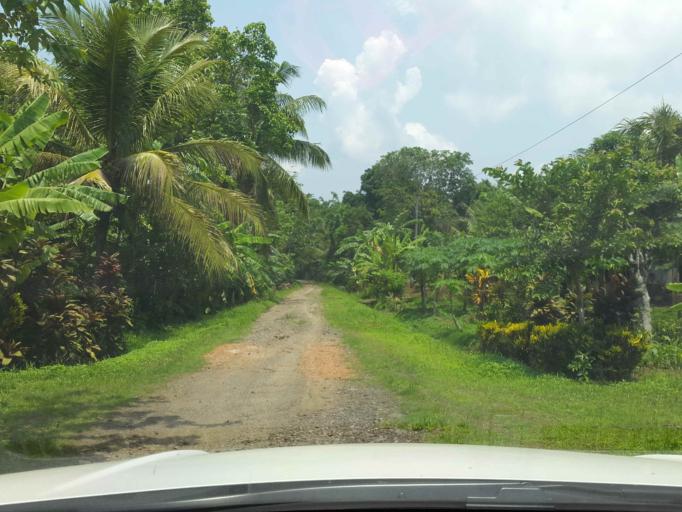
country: ID
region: West Java
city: Cintaratu
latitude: -7.3683
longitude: 108.6920
